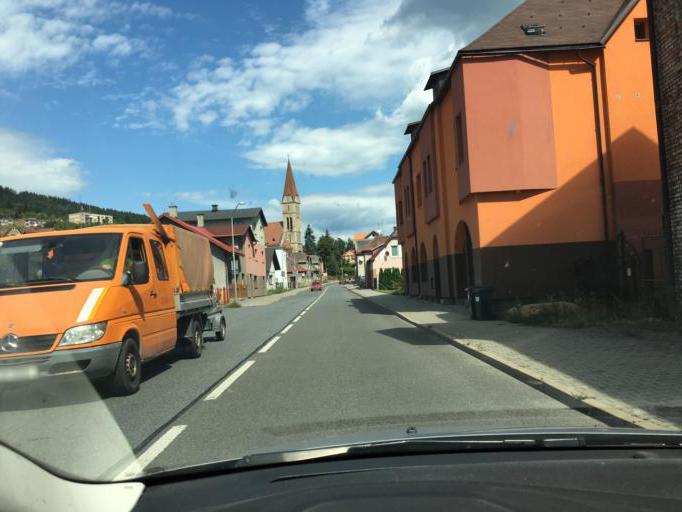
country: CZ
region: Liberecky
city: Velke Hamry
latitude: 50.7151
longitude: 15.3151
